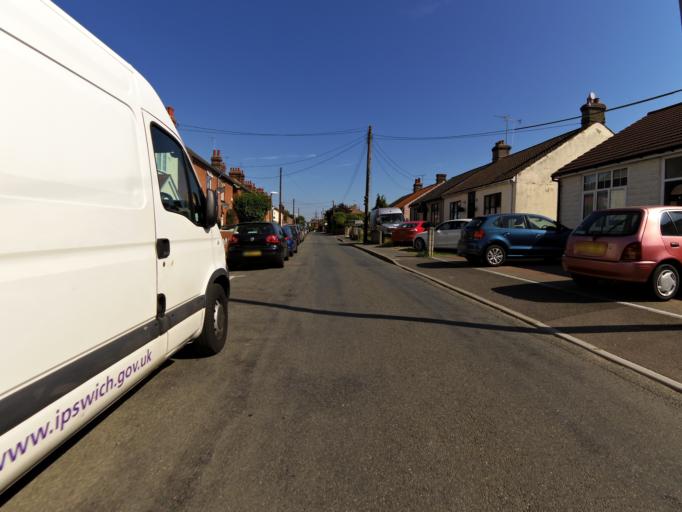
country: GB
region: England
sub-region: Suffolk
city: Bramford
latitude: 52.0769
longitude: 1.1066
